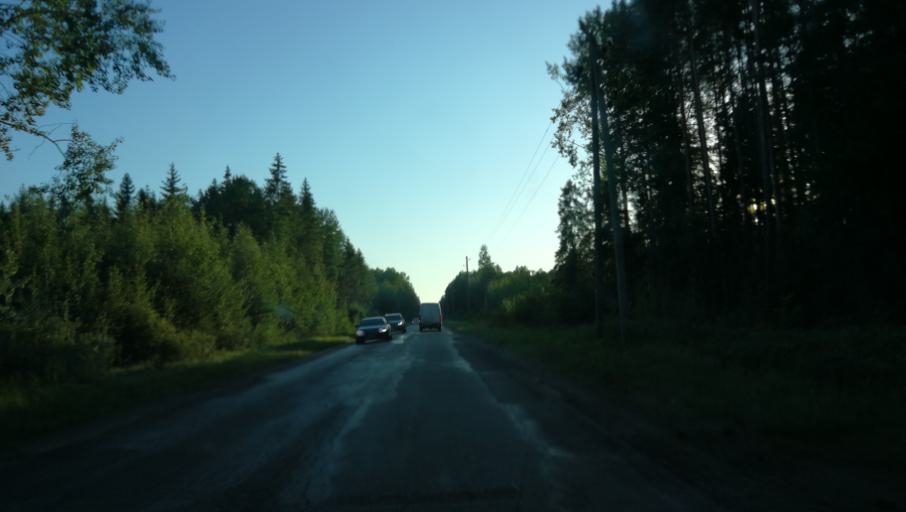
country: LV
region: Saulkrastu
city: Saulkrasti
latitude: 57.2715
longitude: 24.4840
